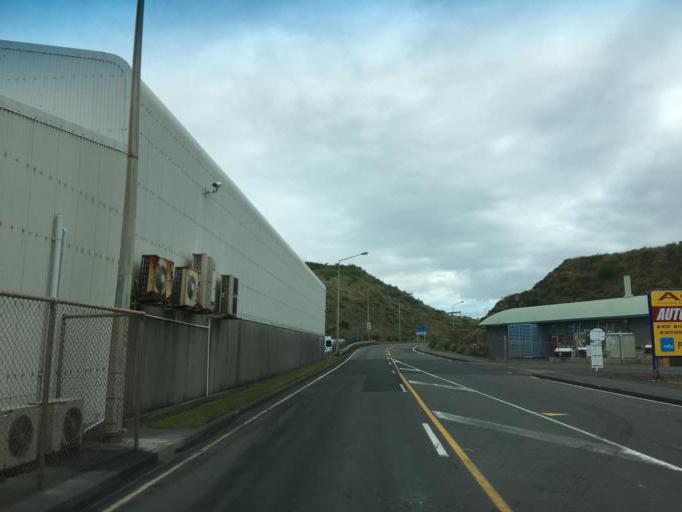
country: NZ
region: Wellington
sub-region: Wellington City
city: Wellington
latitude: -41.3355
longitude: 174.8097
